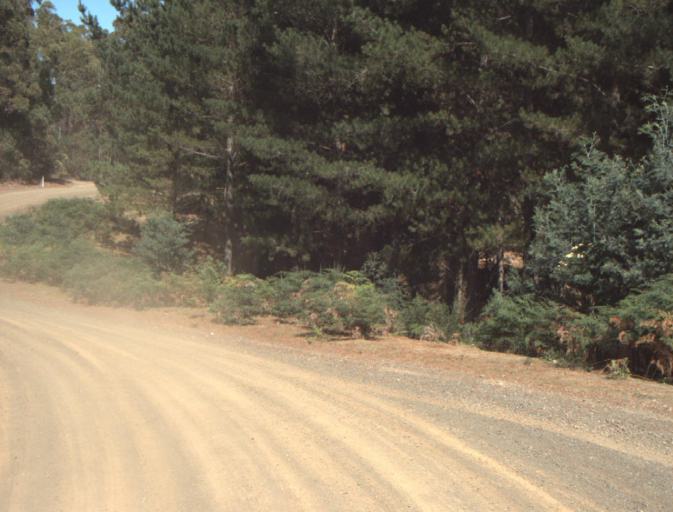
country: AU
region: Tasmania
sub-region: Dorset
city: Scottsdale
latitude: -41.2794
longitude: 147.3407
